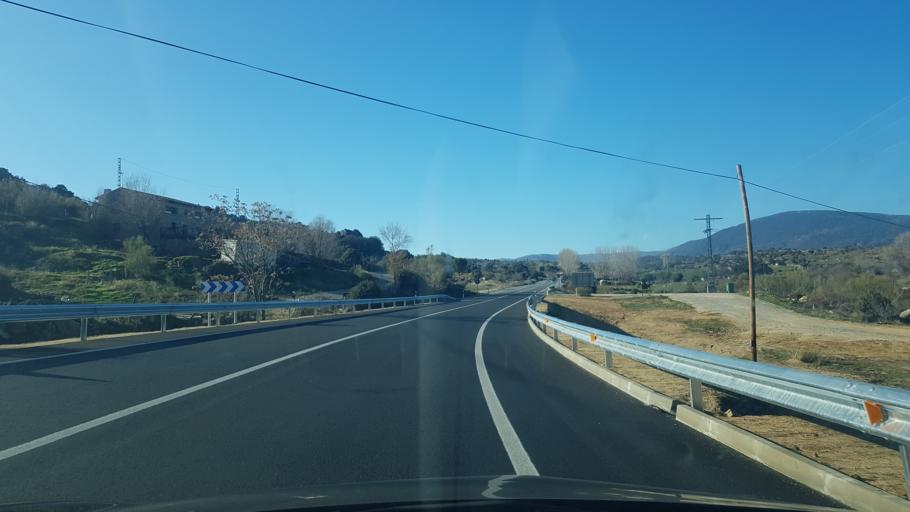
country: ES
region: Castille and Leon
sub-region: Provincia de Avila
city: El Tiemblo
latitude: 40.4446
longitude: -4.5676
